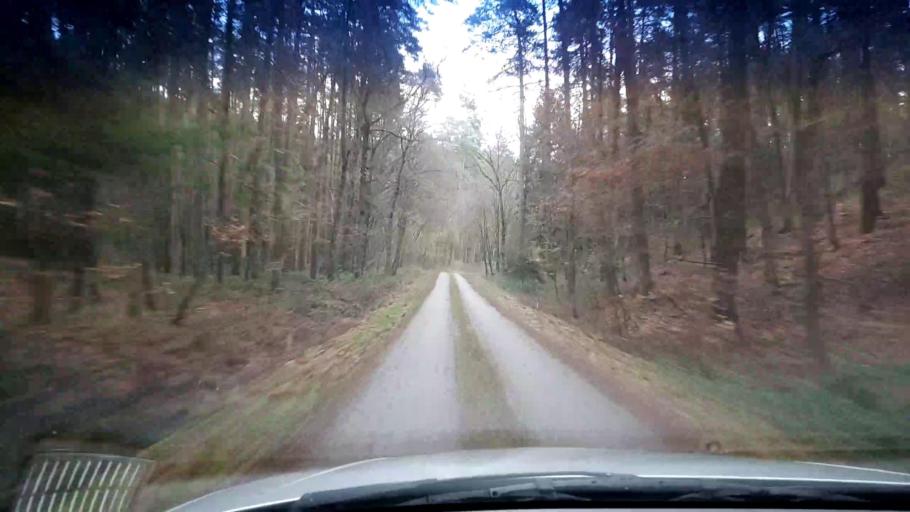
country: DE
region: Bavaria
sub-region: Upper Franconia
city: Lauter
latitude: 49.9443
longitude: 10.7856
